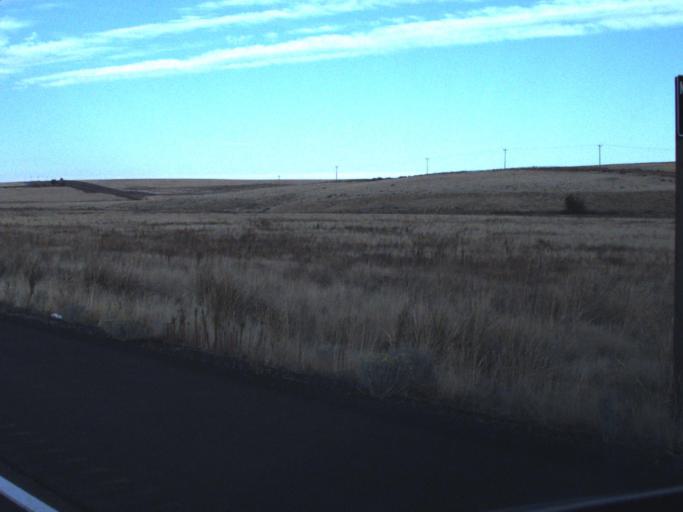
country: US
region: Washington
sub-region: Franklin County
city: Connell
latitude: 46.8203
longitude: -118.6834
